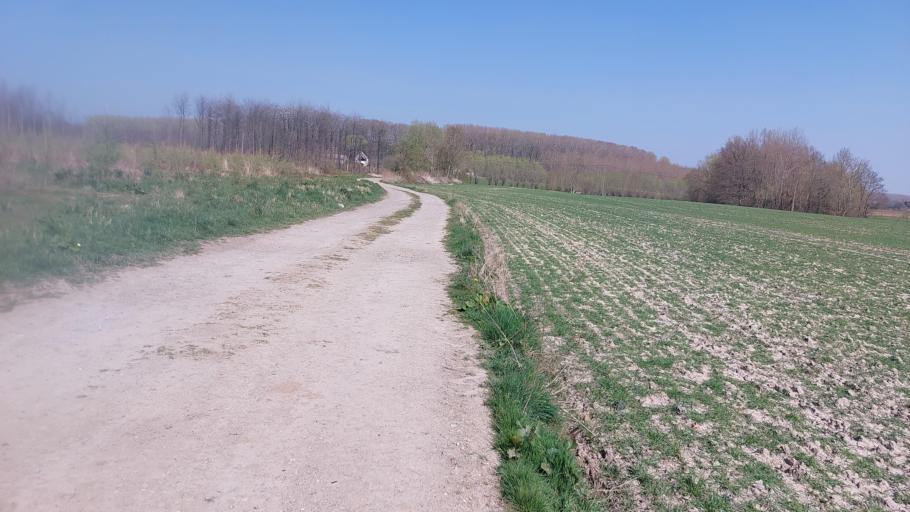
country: BE
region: Wallonia
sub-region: Province du Hainaut
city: Soignies
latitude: 50.5340
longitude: 4.0238
